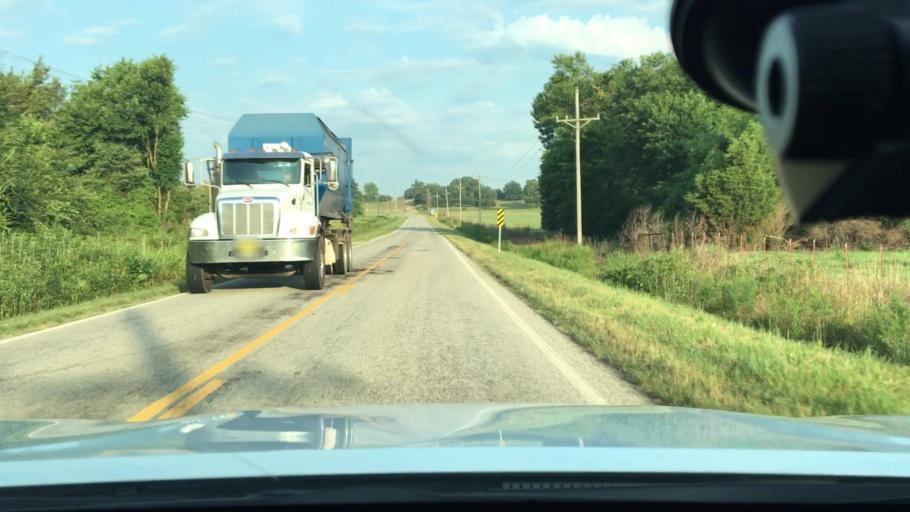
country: US
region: Arkansas
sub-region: Johnson County
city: Coal Hill
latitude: 35.3376
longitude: -93.6256
